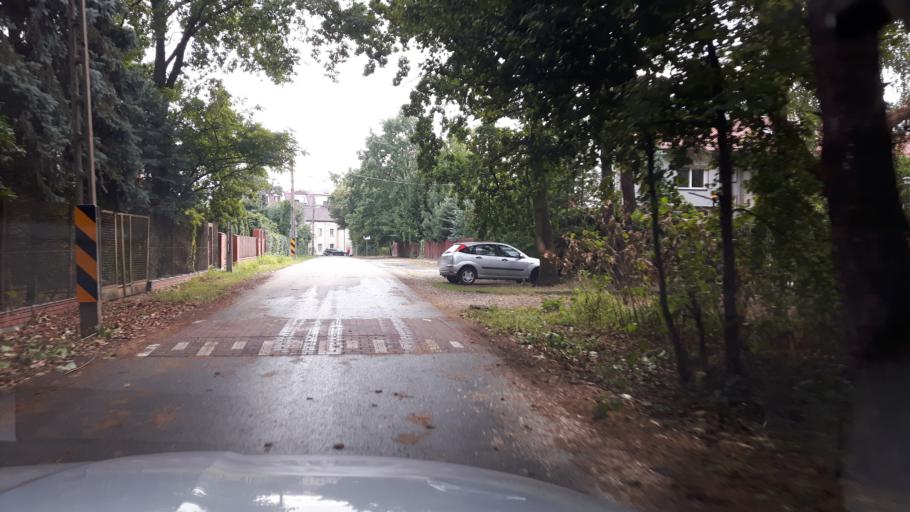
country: PL
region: Masovian Voivodeship
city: Zielonka
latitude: 52.3159
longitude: 21.1558
